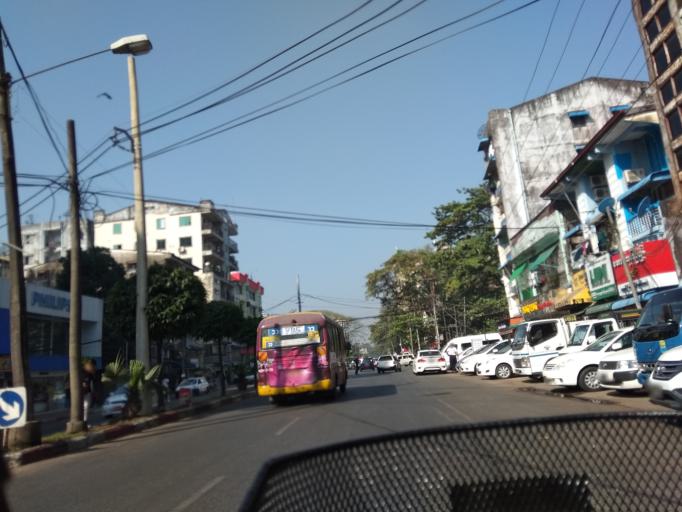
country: MM
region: Yangon
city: Yangon
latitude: 16.8038
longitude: 96.1343
